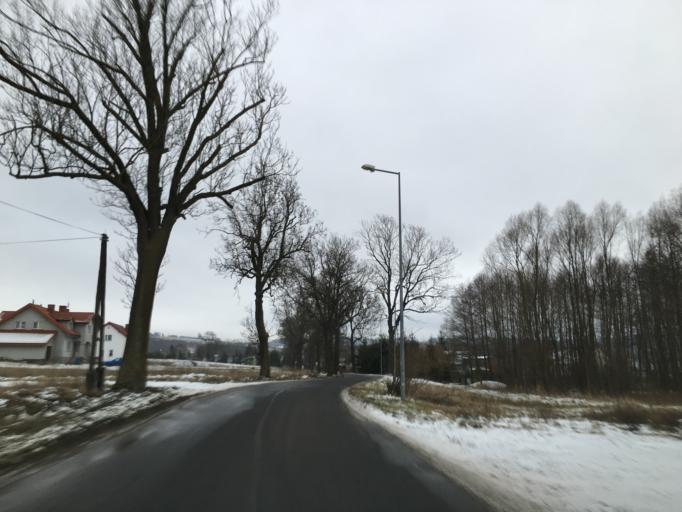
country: PL
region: Lower Silesian Voivodeship
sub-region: Powiat kamiennogorski
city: Krzeszow
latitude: 50.7067
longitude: 16.1125
